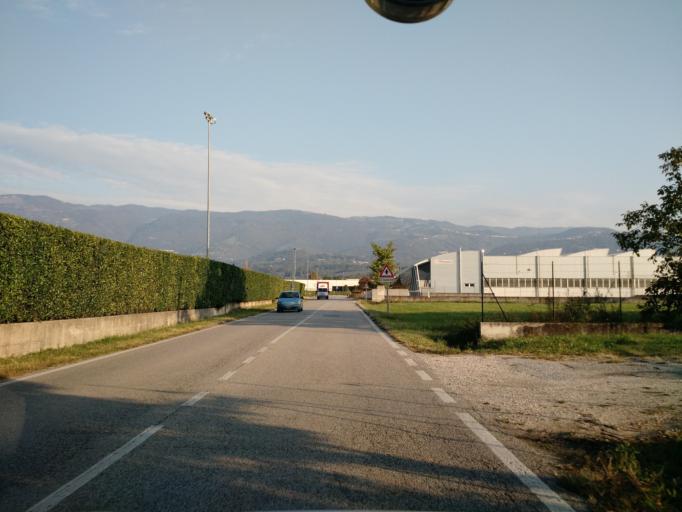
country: IT
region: Veneto
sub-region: Provincia di Vicenza
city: Zugliano
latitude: 45.7246
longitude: 11.5421
